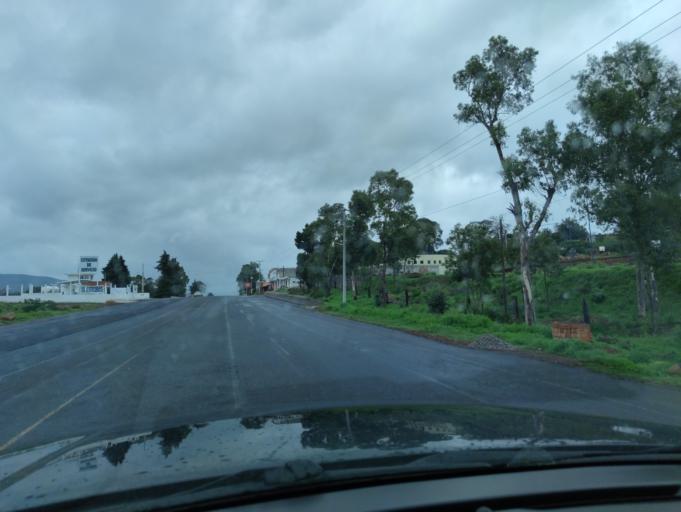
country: MX
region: Mexico
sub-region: Jilotepec
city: Doxhicho
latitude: 19.8927
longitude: -99.6260
